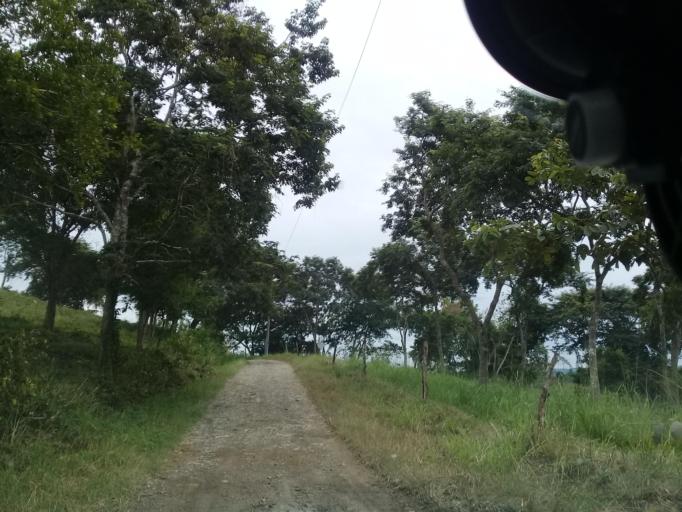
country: MX
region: Hidalgo
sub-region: Huejutla de Reyes
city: Parque de Poblamiento Solidaridad
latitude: 21.1779
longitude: -98.3784
